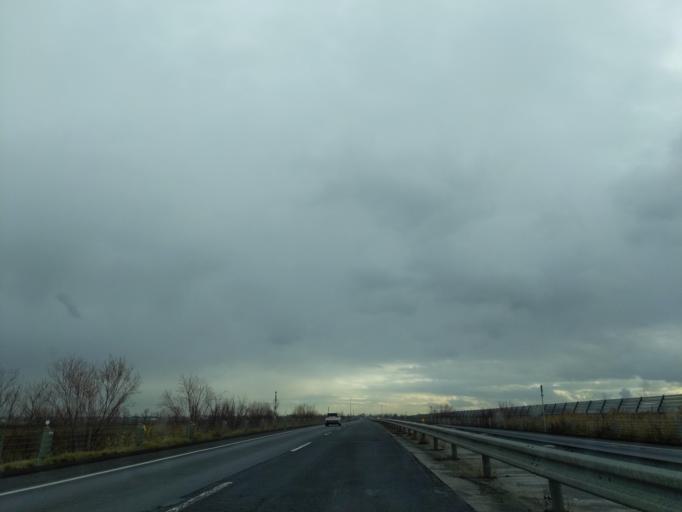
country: JP
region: Hokkaido
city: Ebetsu
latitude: 43.1501
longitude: 141.5656
